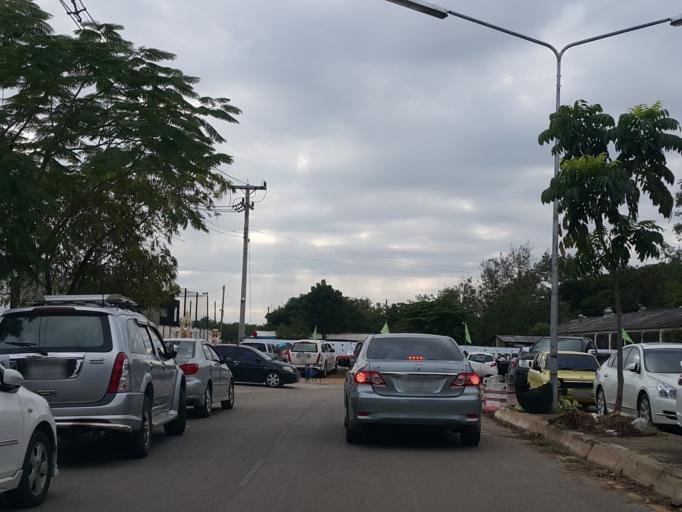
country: TH
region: Lampang
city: Lampang
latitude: 18.2720
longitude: 99.4829
